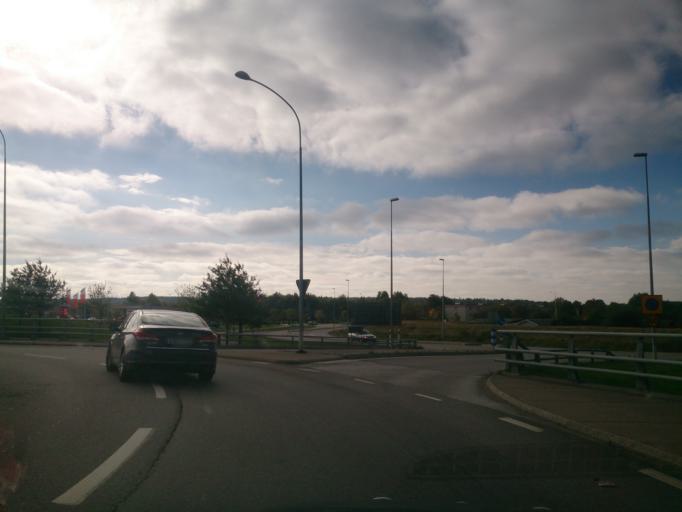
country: SE
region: OEstergoetland
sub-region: Linkopings Kommun
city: Linkoping
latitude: 58.4341
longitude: 15.5829
